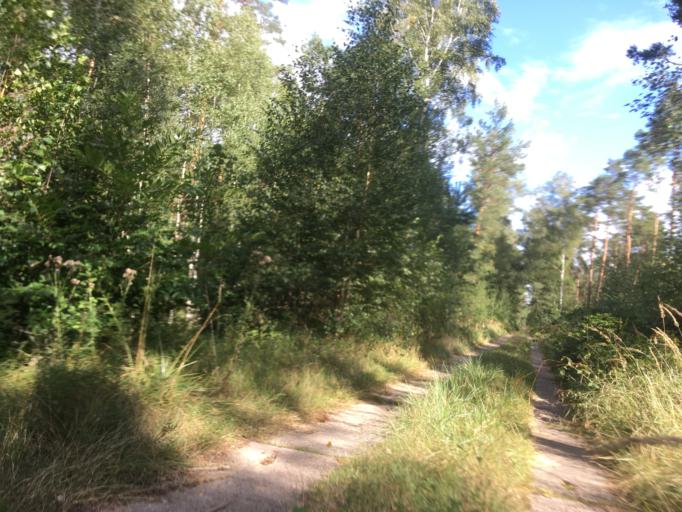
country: DE
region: Brandenburg
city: Halbe
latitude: 52.1657
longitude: 13.7487
